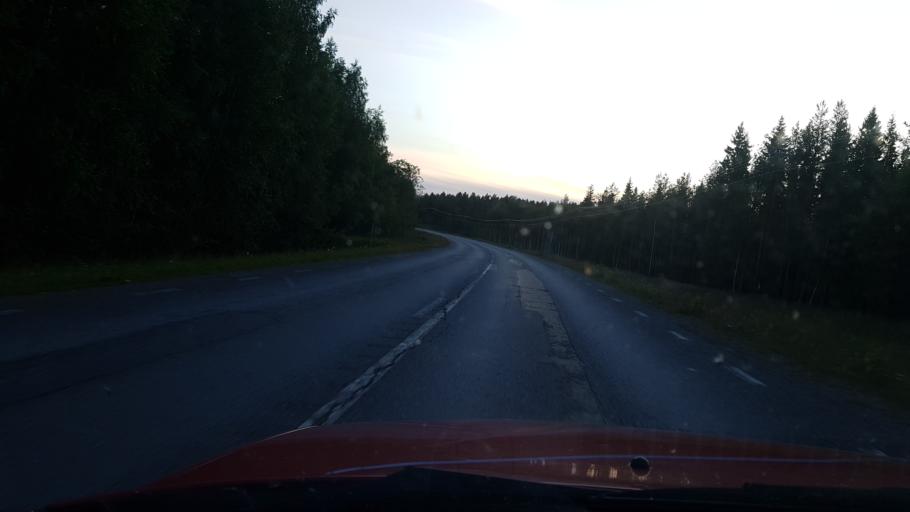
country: SE
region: Norrbotten
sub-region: Alvsbyns Kommun
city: AElvsbyn
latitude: 65.6920
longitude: 20.6835
